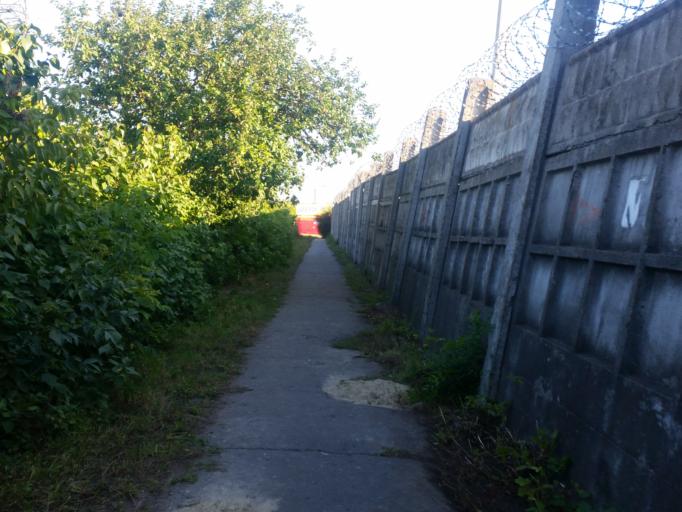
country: RU
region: Ulyanovsk
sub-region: Ulyanovskiy Rayon
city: Ulyanovsk
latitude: 54.3323
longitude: 48.3645
